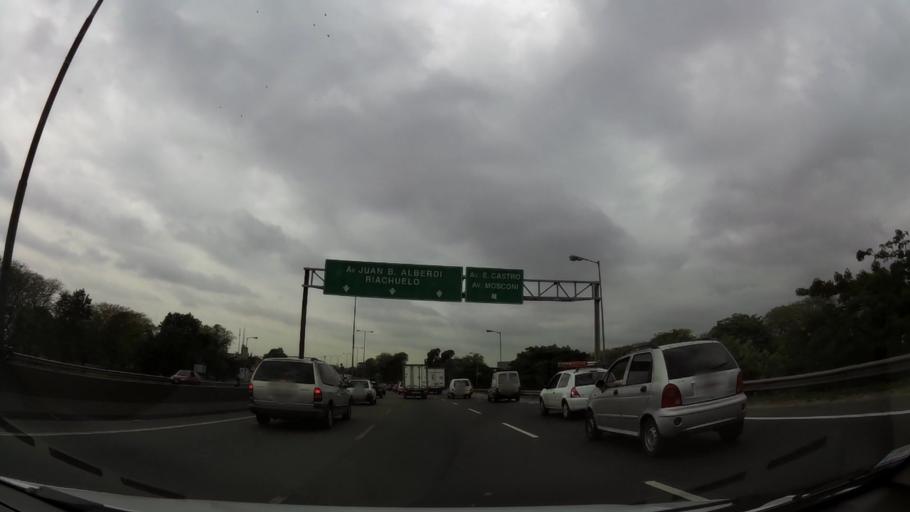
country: AR
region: Buenos Aires
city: San Justo
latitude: -34.6543
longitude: -58.5282
